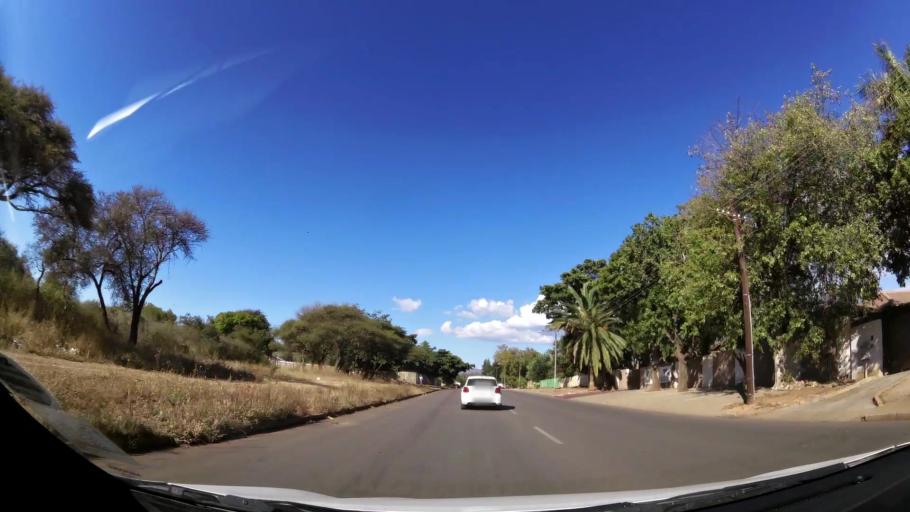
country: ZA
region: Limpopo
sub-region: Waterberg District Municipality
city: Mokopane
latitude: -24.1759
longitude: 29.0072
